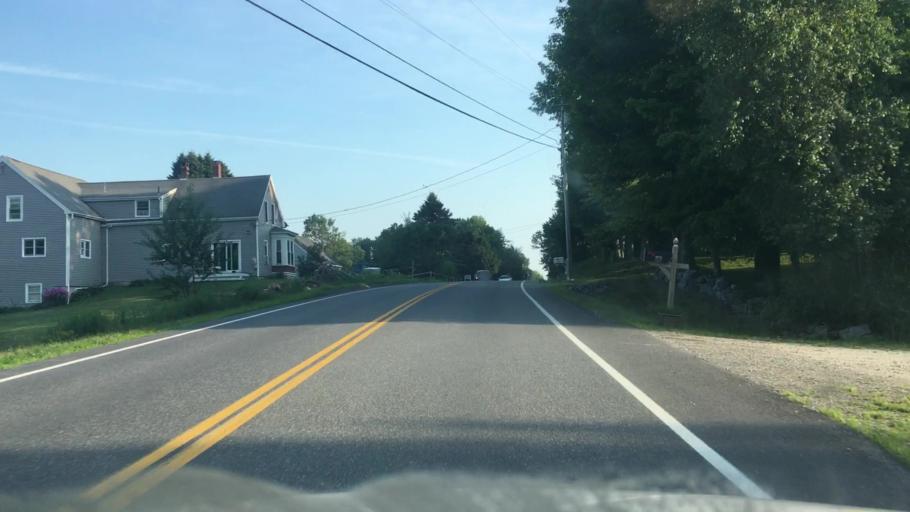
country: US
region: Maine
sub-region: Cumberland County
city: Freeport
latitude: 43.9156
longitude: -70.0904
